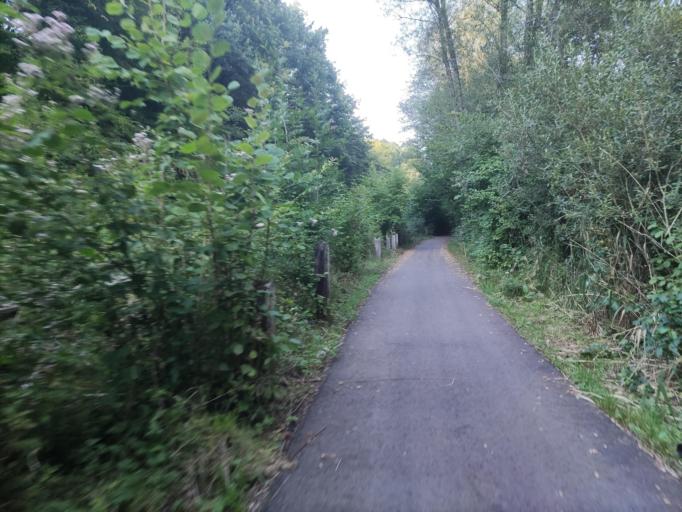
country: DE
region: Saarland
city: Wadgassen
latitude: 49.2557
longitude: 6.7958
